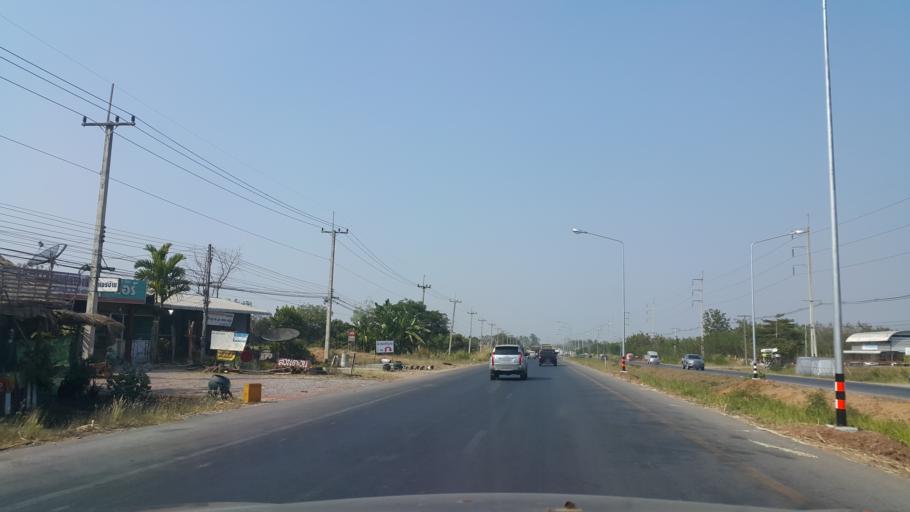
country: TH
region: Chaiyaphum
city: Phu Khiao
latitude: 16.4272
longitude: 102.1294
